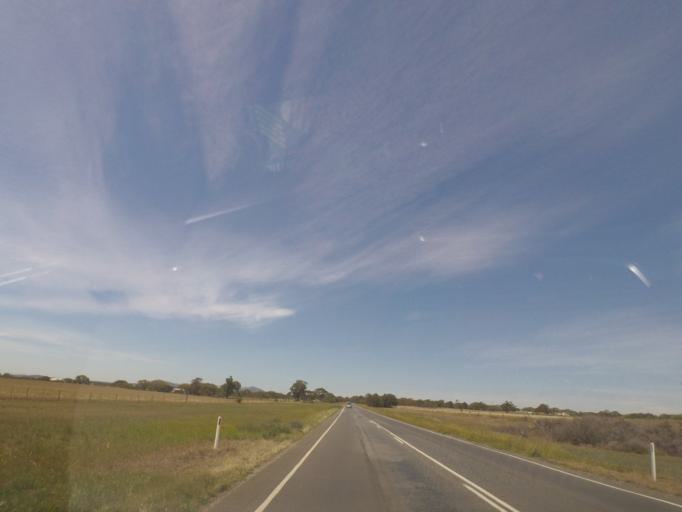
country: AU
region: Victoria
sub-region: Wyndham
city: Wyndham Vale
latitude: -37.8481
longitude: 144.3872
